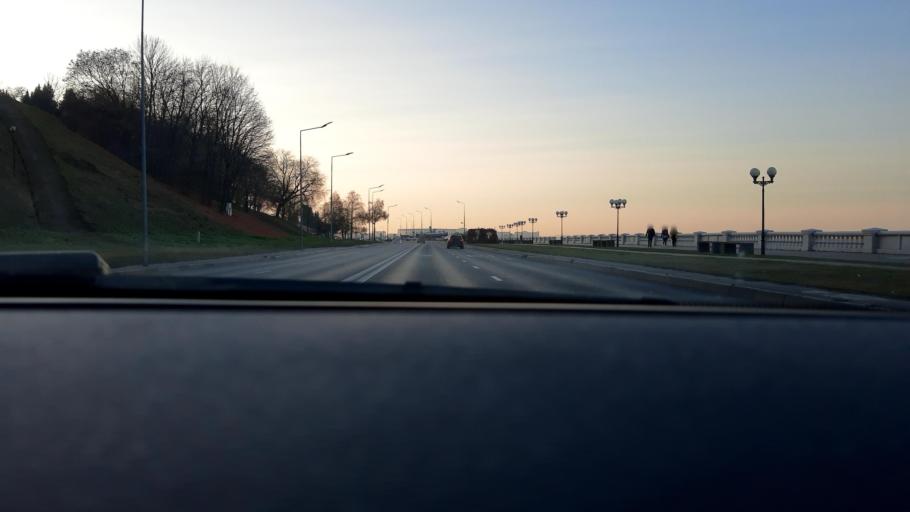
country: RU
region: Nizjnij Novgorod
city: Nizhniy Novgorod
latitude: 56.3321
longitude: 44.0184
